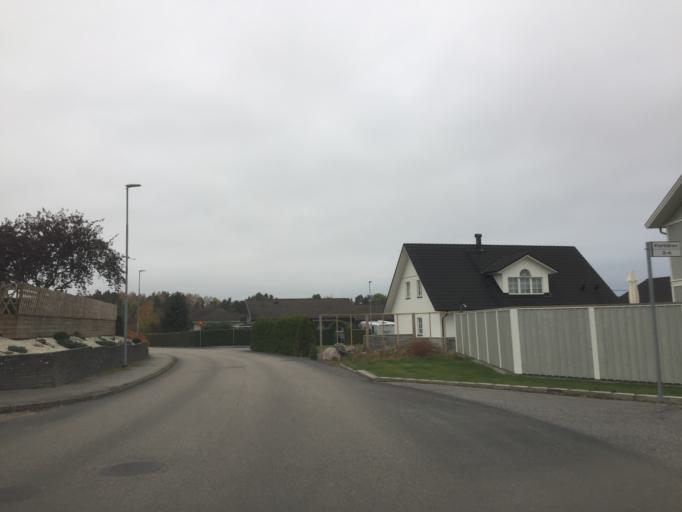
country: SE
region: Vaestra Goetaland
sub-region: Trollhattan
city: Trollhattan
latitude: 58.2912
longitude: 12.3499
